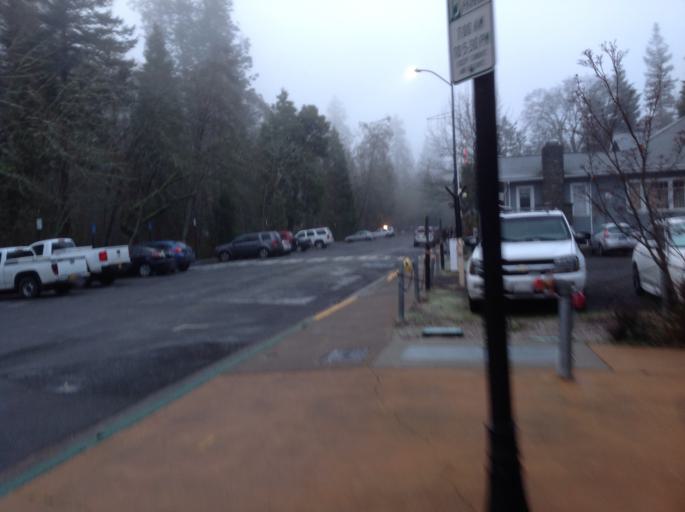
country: US
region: Oregon
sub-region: Jackson County
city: Ashland
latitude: 42.1963
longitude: -122.7164
